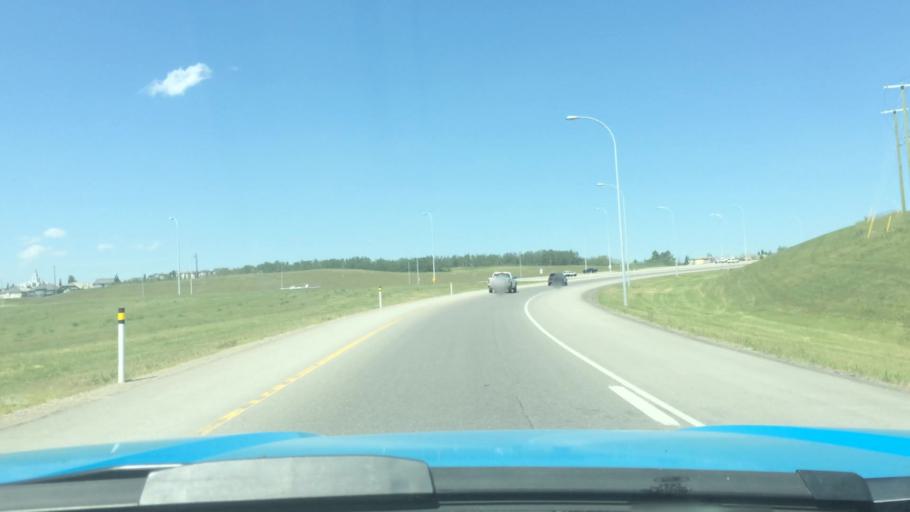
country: CA
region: Alberta
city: Calgary
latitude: 51.1318
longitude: -114.2234
